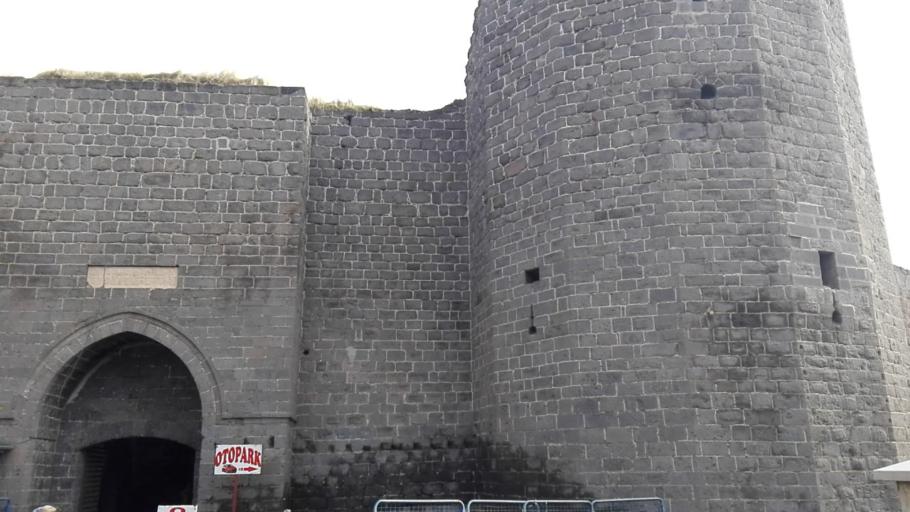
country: TR
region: Diyarbakir
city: Sur
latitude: 37.9148
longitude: 40.2401
